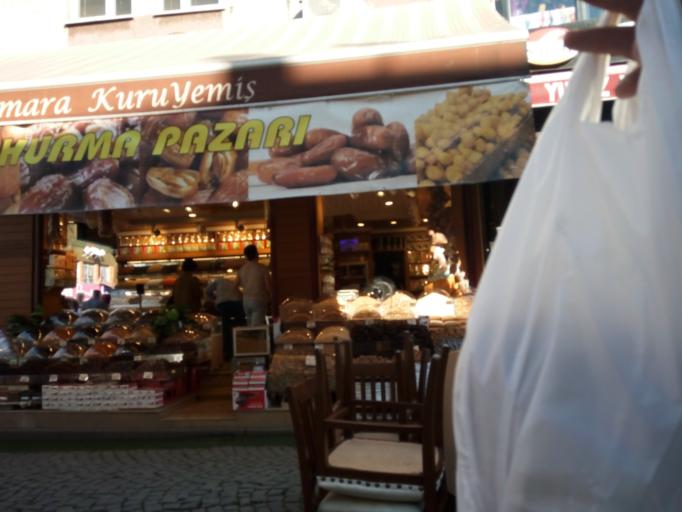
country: TR
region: Istanbul
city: UEskuedar
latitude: 41.0253
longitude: 29.0169
